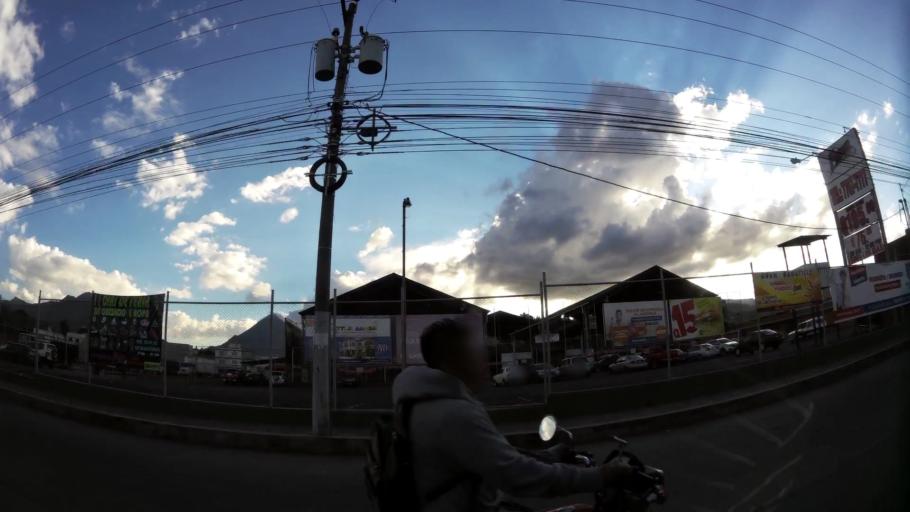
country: GT
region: Quetzaltenango
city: Quetzaltenango
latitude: 14.8514
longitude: -91.5314
